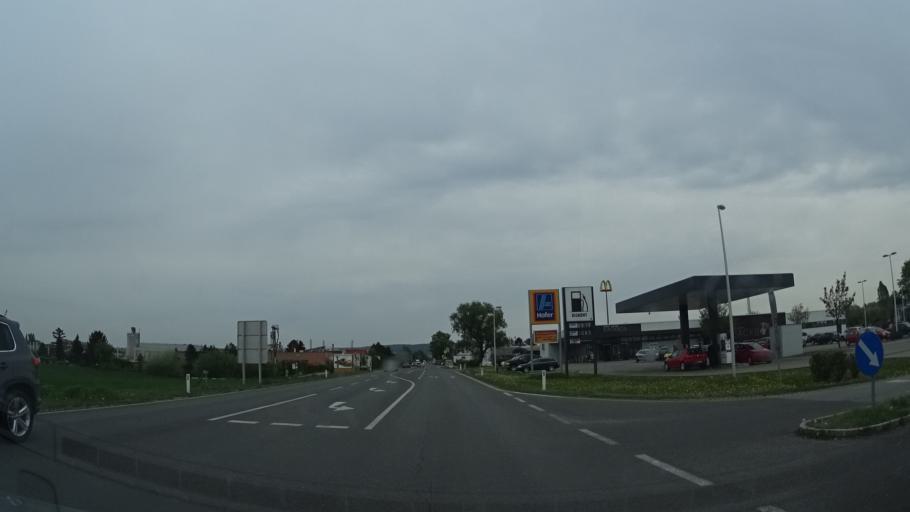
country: AT
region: Lower Austria
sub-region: Politischer Bezirk Korneuburg
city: Leobendorf
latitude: 48.3607
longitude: 16.3108
